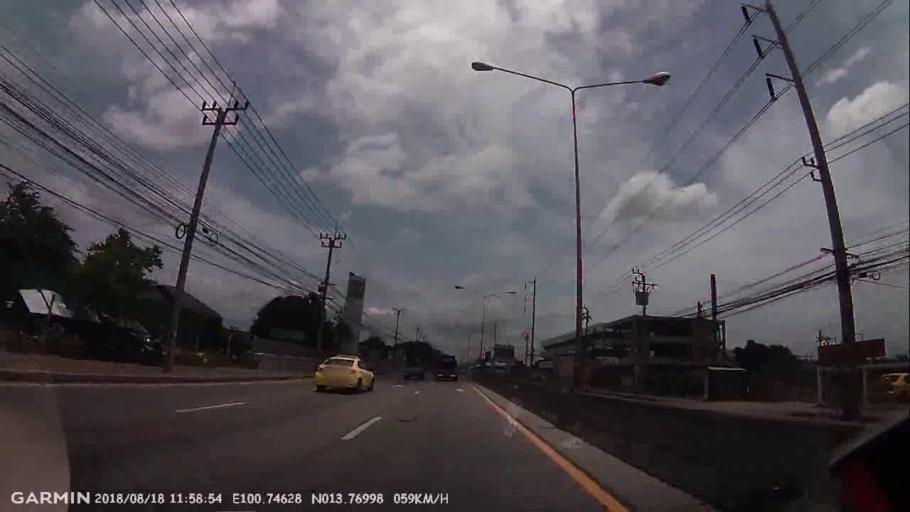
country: TH
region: Bangkok
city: Min Buri
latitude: 13.7701
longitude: 100.7463
